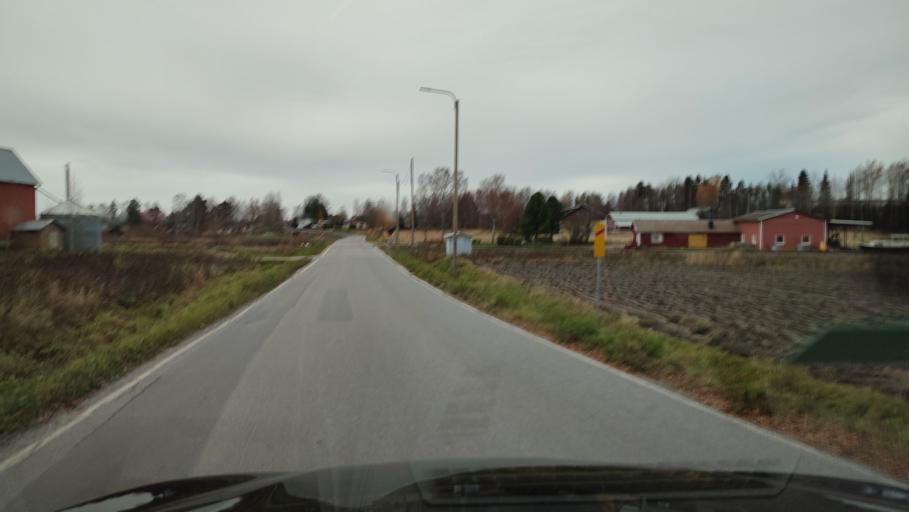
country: FI
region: Ostrobothnia
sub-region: Sydosterbotten
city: Naerpes
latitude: 62.4714
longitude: 21.3733
